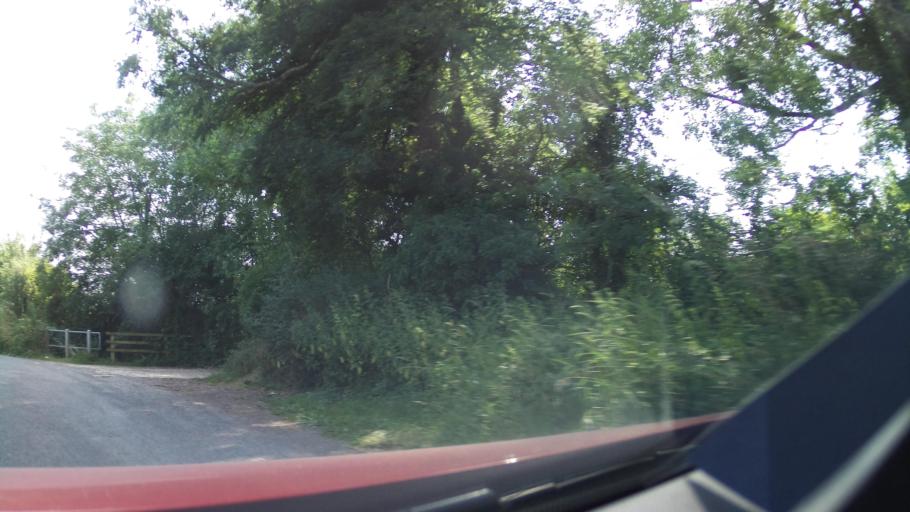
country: GB
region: England
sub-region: Wiltshire
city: Minety
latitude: 51.6437
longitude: -1.9763
